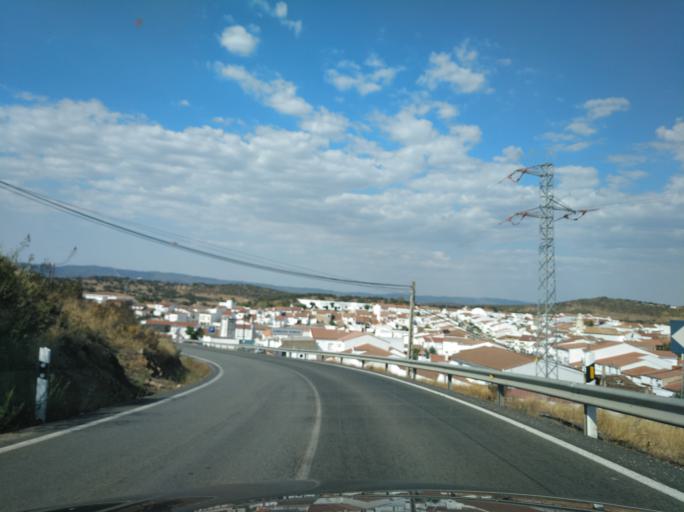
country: ES
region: Andalusia
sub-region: Provincia de Huelva
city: Cabezas Rubias
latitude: 37.7248
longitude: -7.0893
